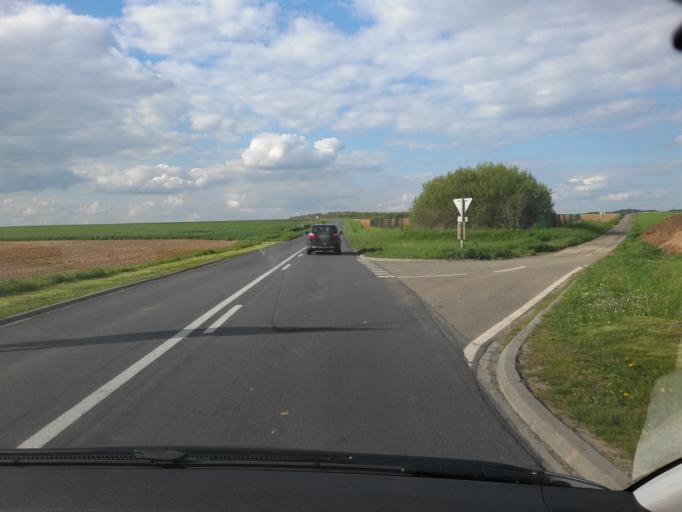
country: FR
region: Picardie
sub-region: Departement de l'Oise
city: Grandfresnoy
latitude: 49.3869
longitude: 2.6567
